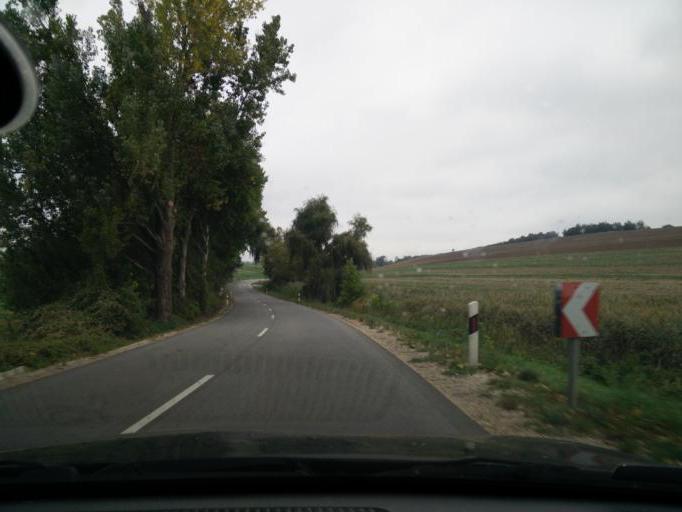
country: HU
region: Komarom-Esztergom
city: Bajna
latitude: 47.6656
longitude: 18.6056
